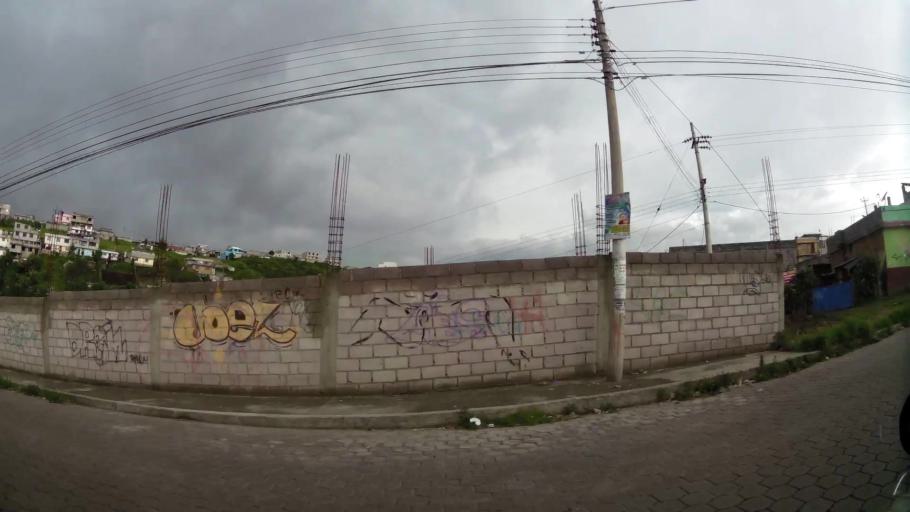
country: EC
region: Pichincha
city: Quito
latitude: -0.2970
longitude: -78.5246
